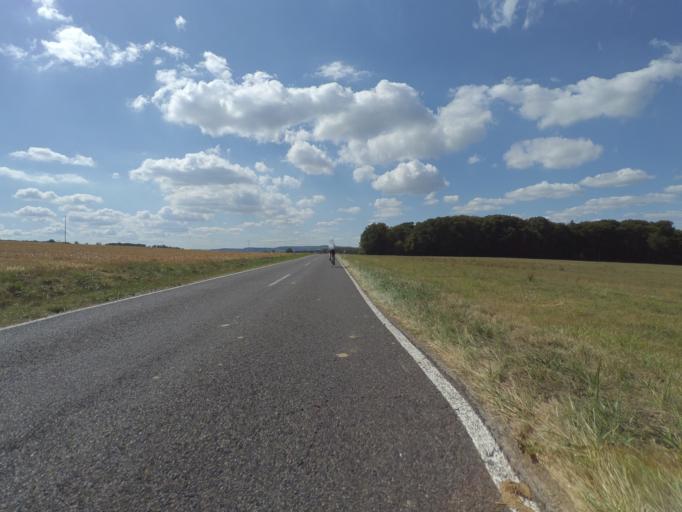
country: DE
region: Rheinland-Pfalz
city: Palzem
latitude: 49.5734
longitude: 6.4003
